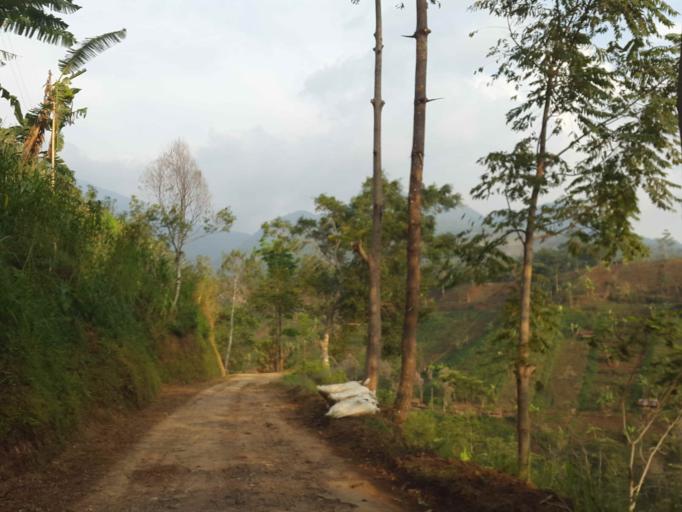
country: ID
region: Central Java
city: Jatiroto
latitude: -7.7055
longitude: 111.1262
